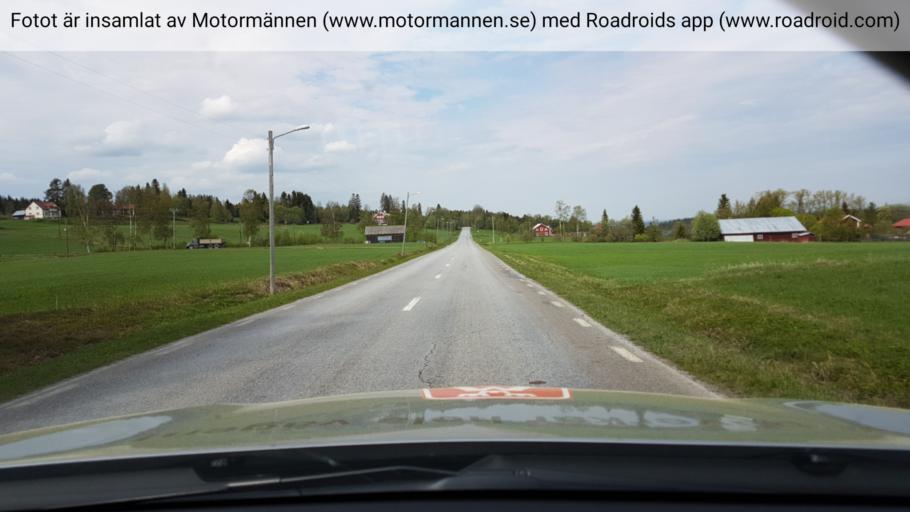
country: SE
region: Jaemtland
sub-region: Krokoms Kommun
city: Krokom
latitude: 63.1458
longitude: 14.1741
